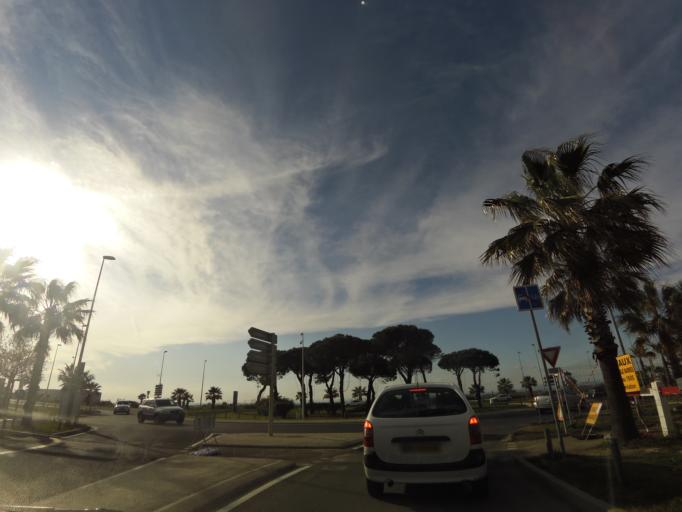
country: FR
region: Languedoc-Roussillon
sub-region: Departement de l'Herault
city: Palavas-les-Flots
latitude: 43.5321
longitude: 3.9267
